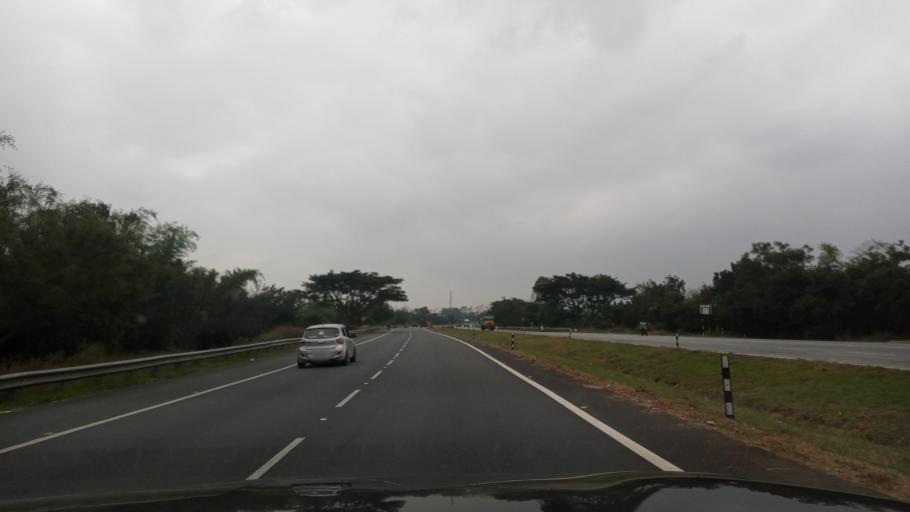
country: IN
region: Karnataka
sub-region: Bangalore Rural
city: Nelamangala
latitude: 13.0227
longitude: 77.4756
